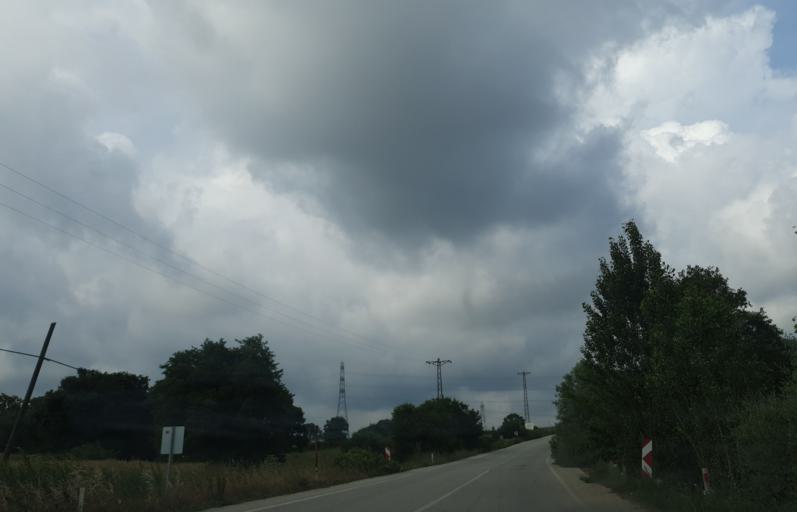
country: TR
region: Tekirdag
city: Saray
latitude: 41.4784
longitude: 27.9577
